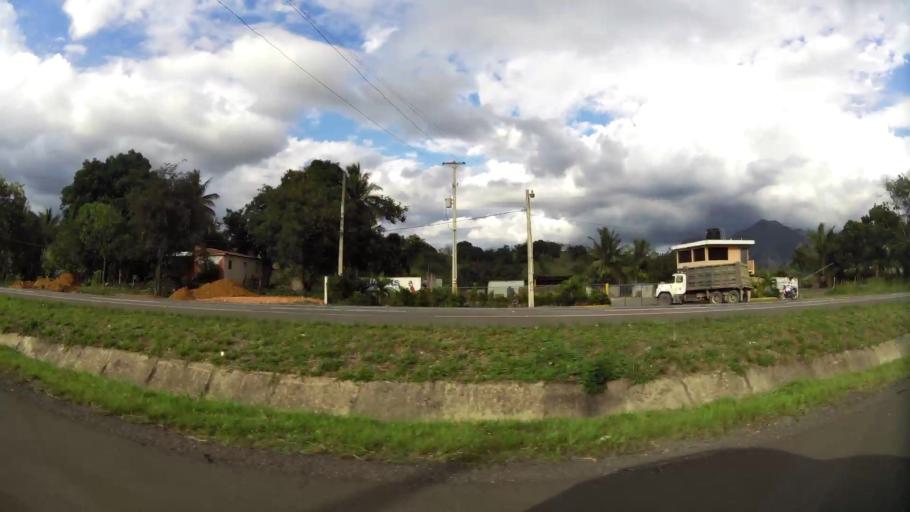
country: DO
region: Monsenor Nouel
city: Piedra Blanca
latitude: 18.8504
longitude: -70.3265
